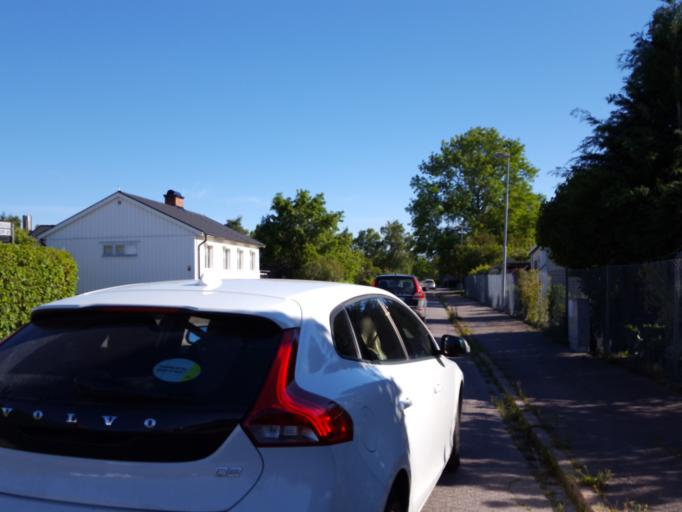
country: SE
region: Uppsala
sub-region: Uppsala Kommun
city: Uppsala
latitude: 59.8613
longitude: 17.6686
